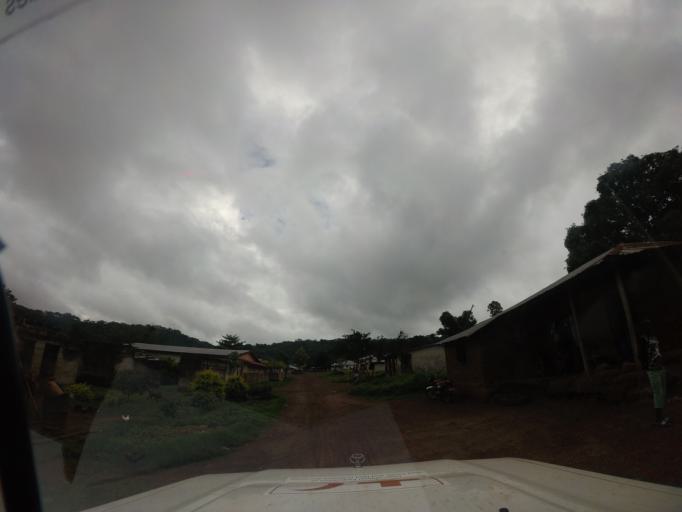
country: SL
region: Northern Province
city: Kamakwie
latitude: 9.6752
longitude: -12.2249
